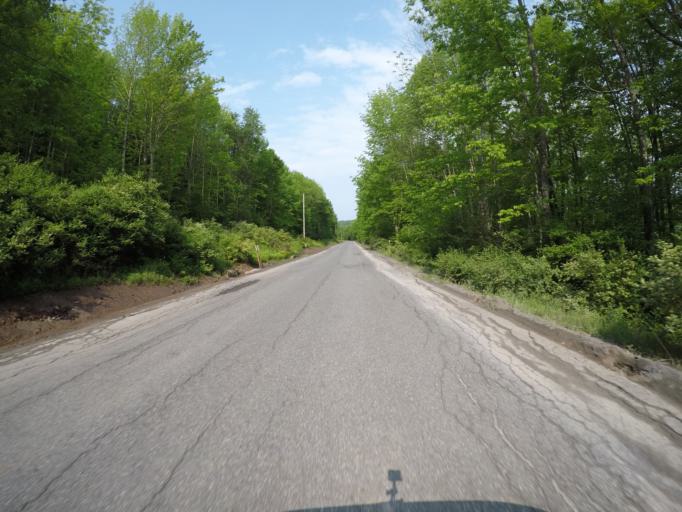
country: US
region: New York
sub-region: Sullivan County
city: Livingston Manor
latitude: 42.1126
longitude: -74.7595
